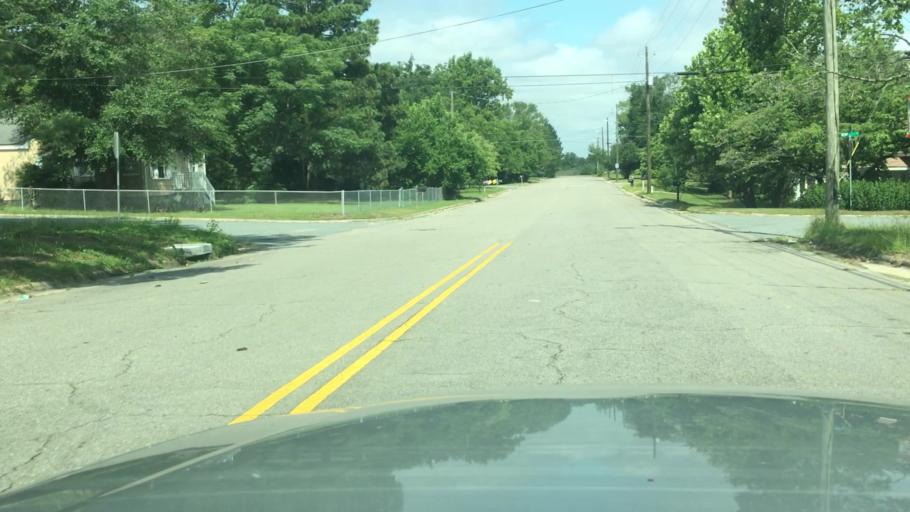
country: US
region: North Carolina
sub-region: Cumberland County
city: Fayetteville
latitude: 35.0244
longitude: -78.9009
